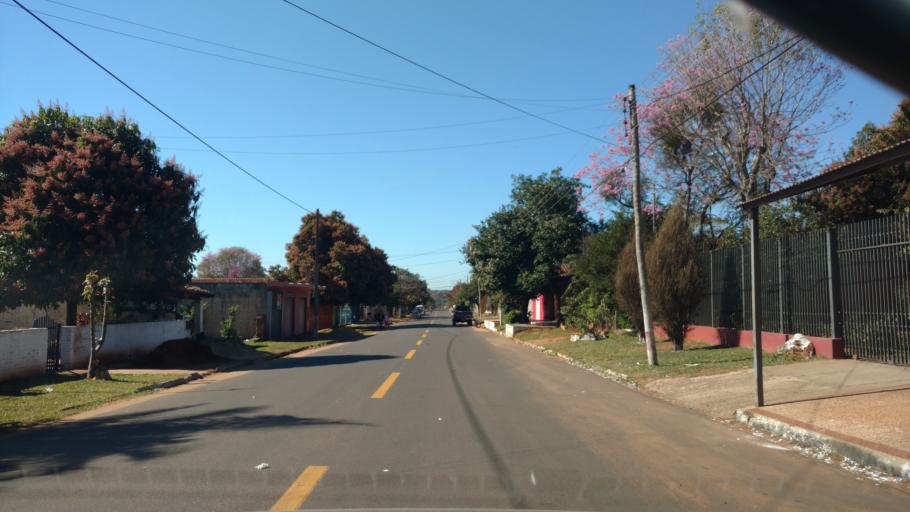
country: PY
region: Central
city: Capiata
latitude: -25.3695
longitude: -57.4101
